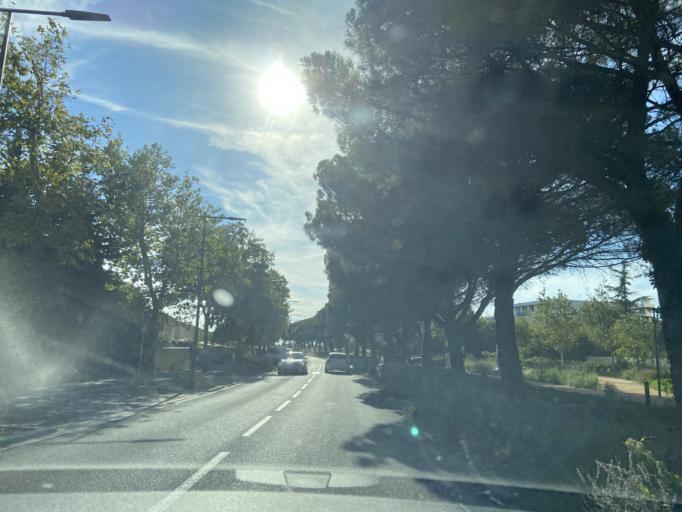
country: FR
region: Provence-Alpes-Cote d'Azur
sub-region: Departement des Bouches-du-Rhone
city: Miramas
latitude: 43.5882
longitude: 4.9974
